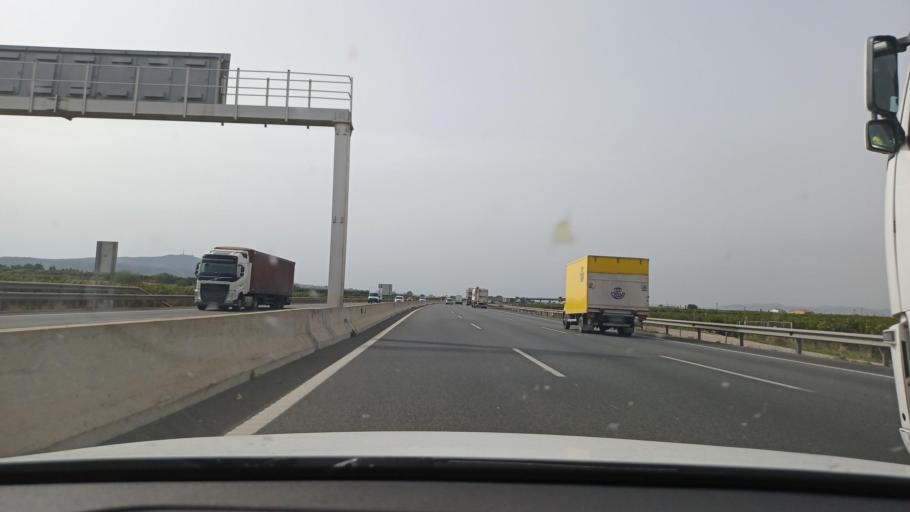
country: ES
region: Valencia
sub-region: Provincia de Valencia
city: Torrent
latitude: 39.4237
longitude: -0.5193
